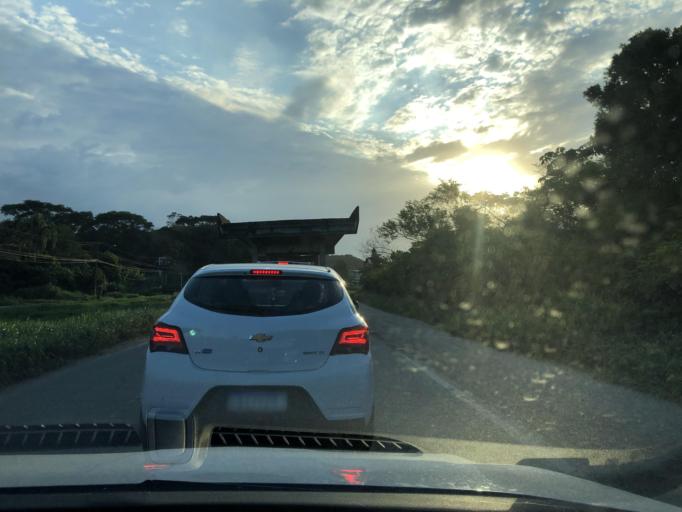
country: BR
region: Santa Catarina
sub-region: Sao Francisco Do Sul
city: Sao Francisco do Sul
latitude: -26.2520
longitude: -48.6113
